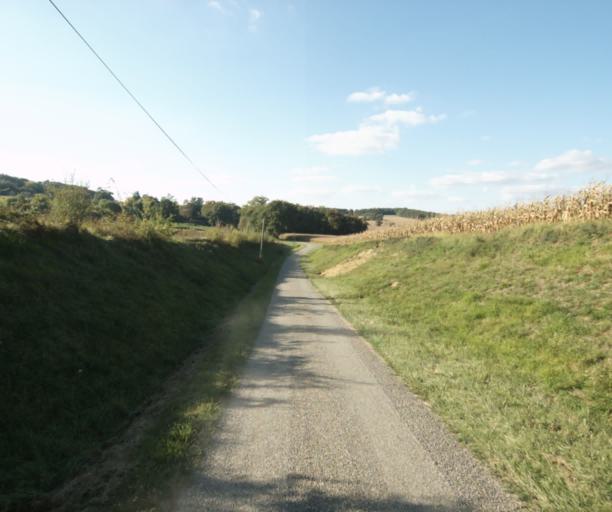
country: FR
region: Midi-Pyrenees
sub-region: Departement du Gers
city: Eauze
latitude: 43.7852
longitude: 0.1316
